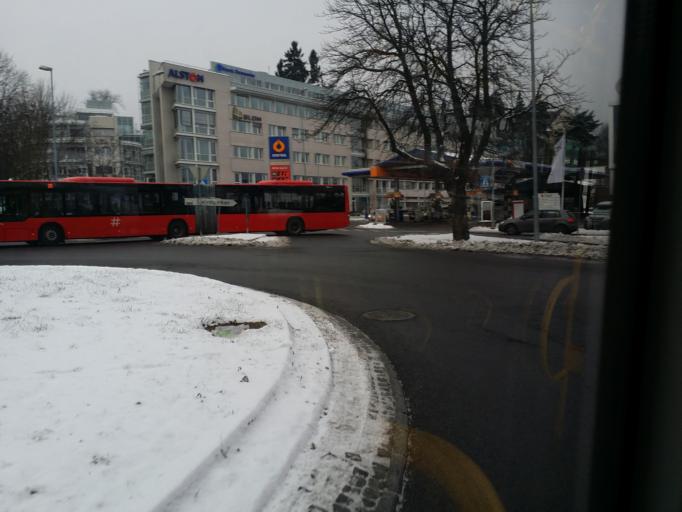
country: NO
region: Oslo
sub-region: Oslo
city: Sjolyststranda
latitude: 59.9214
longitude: 10.6764
